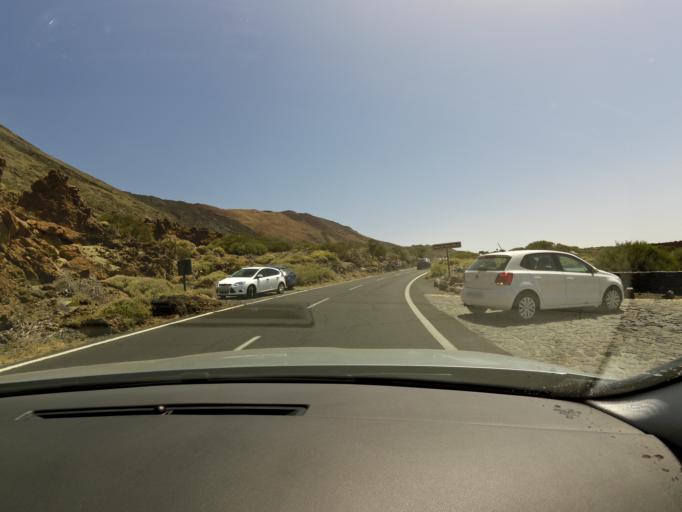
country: ES
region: Canary Islands
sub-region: Provincia de Santa Cruz de Tenerife
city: Vilaflor
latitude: 28.2535
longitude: -16.6250
